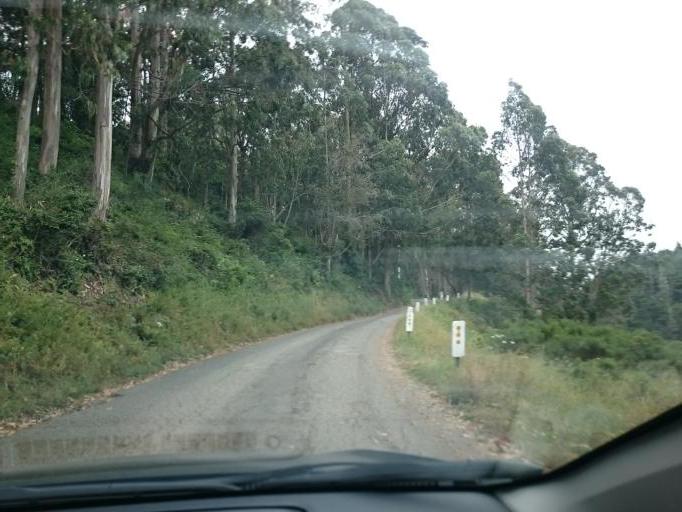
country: US
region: California
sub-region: Mendocino County
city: Fort Bragg
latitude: 39.2267
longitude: -123.7665
